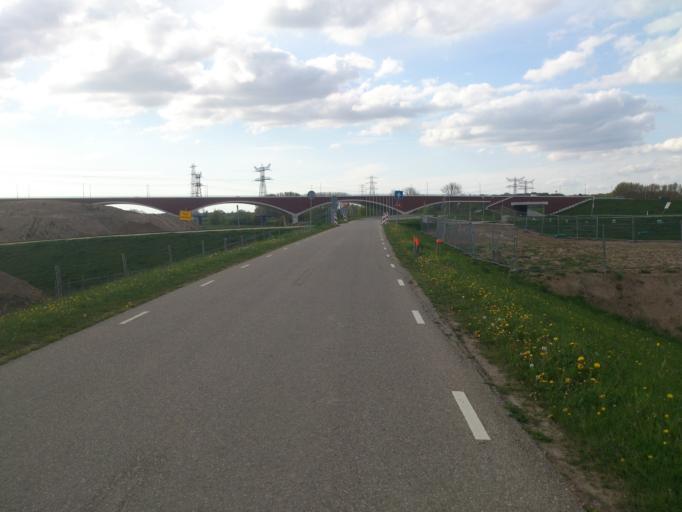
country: NL
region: Gelderland
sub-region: Gemeente Nijmegen
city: Nijmegen
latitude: 51.8624
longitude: 5.8489
